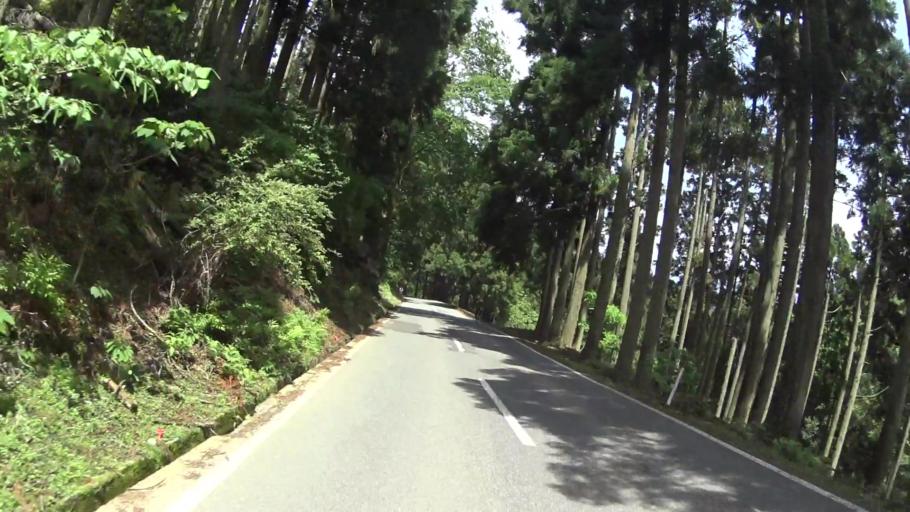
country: JP
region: Kyoto
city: Maizuru
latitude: 35.4424
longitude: 135.4994
